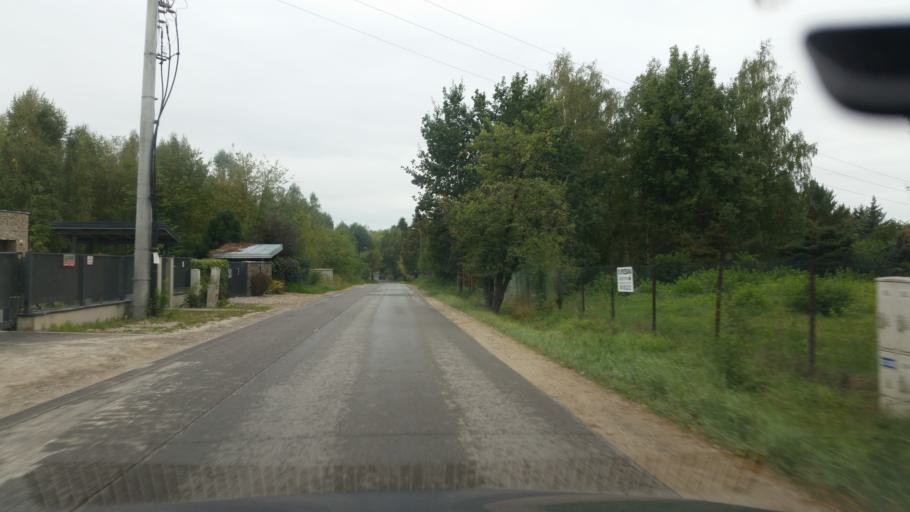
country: PL
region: Masovian Voivodeship
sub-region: Powiat piaseczynski
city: Jozefoslaw
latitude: 52.0933
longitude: 21.0771
